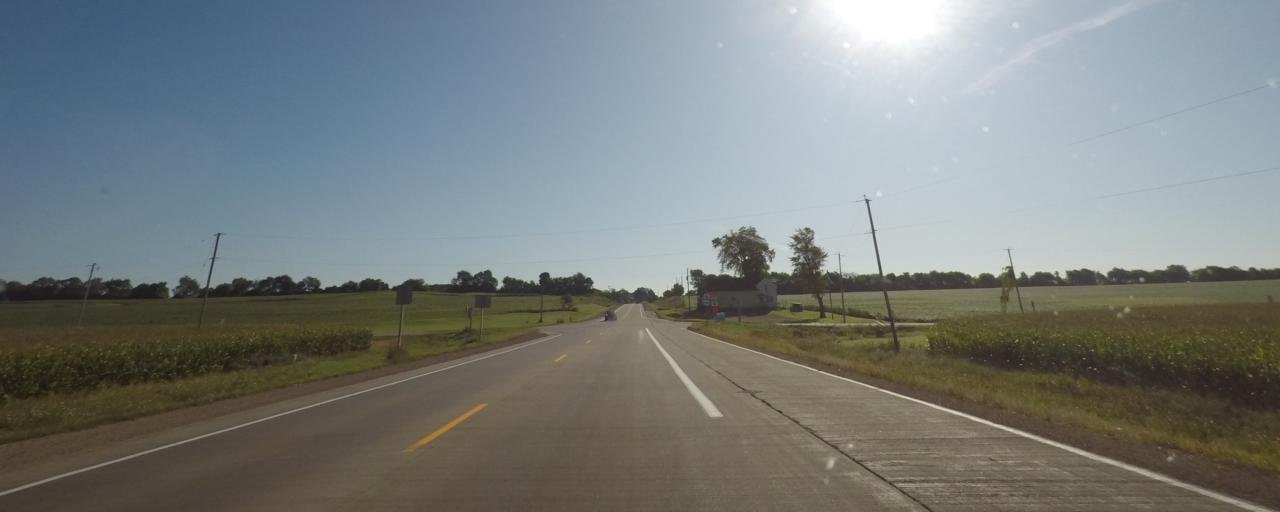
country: US
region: Wisconsin
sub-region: Dane County
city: Deerfield
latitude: 43.0364
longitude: -89.1084
